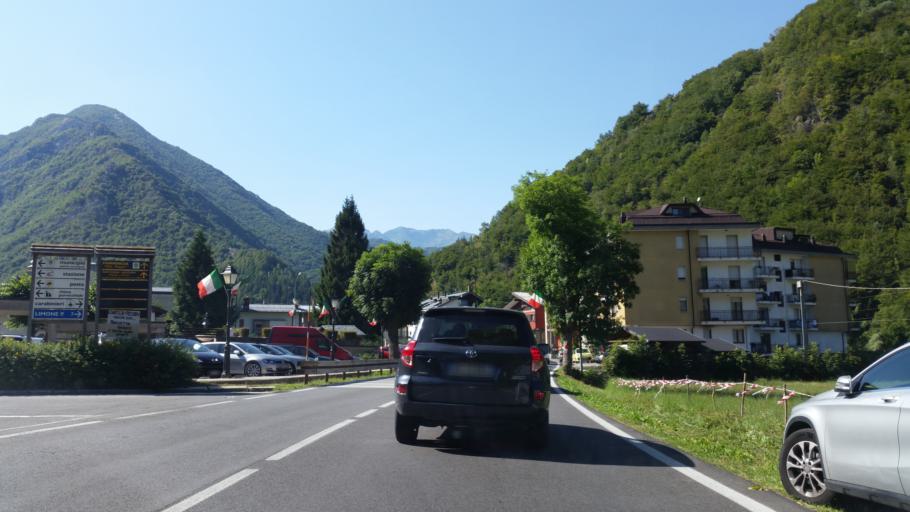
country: IT
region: Piedmont
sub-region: Provincia di Cuneo
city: Vernante
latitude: 44.2482
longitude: 7.5322
